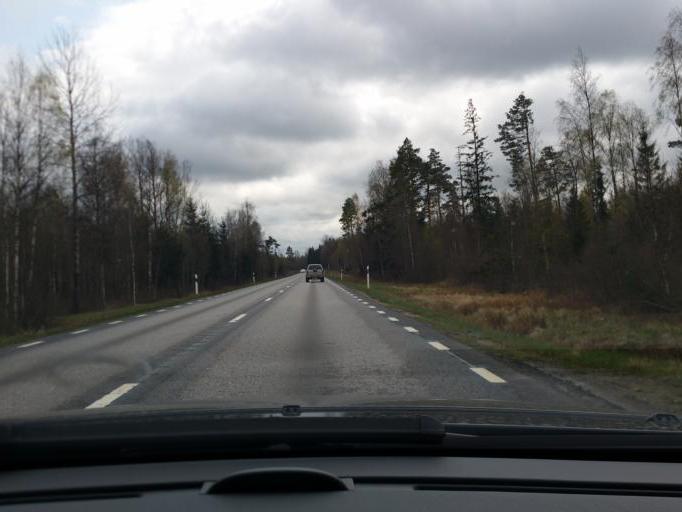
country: SE
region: Kronoberg
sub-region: Vaxjo Kommun
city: Ingelstad
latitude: 56.7902
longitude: 14.8969
